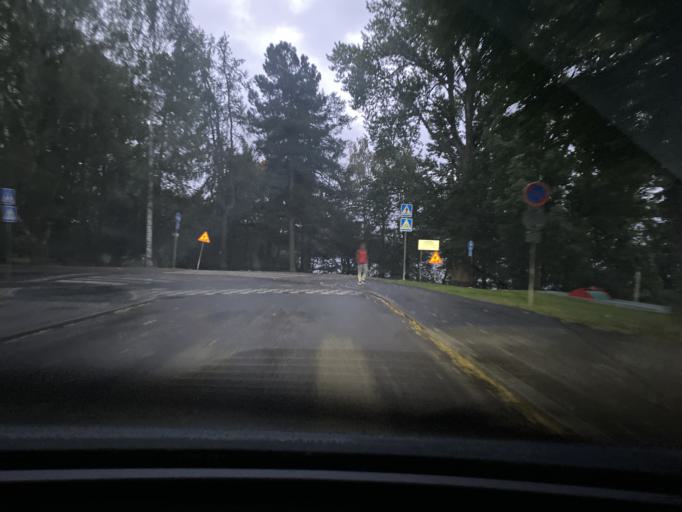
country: FI
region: Pirkanmaa
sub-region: Tampere
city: Tampere
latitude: 61.4911
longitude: 23.7488
